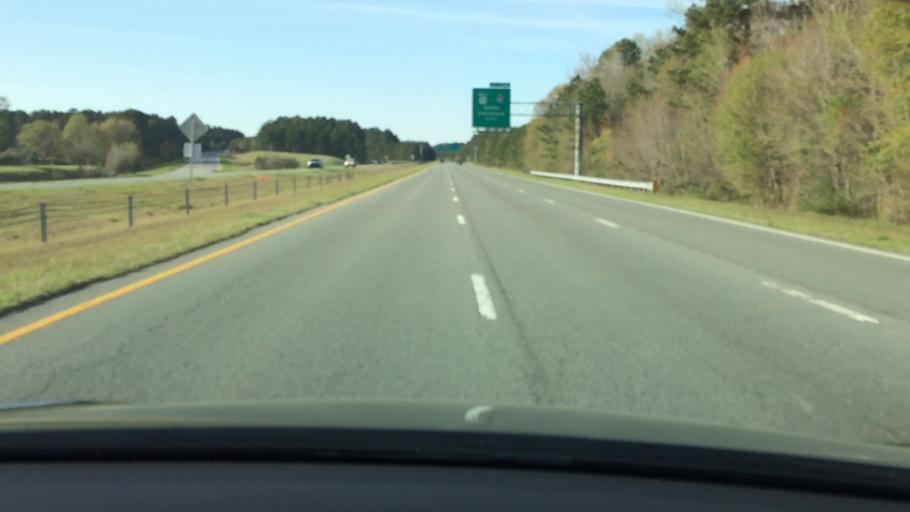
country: US
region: North Carolina
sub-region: Johnston County
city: Selma
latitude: 35.5046
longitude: -78.2810
